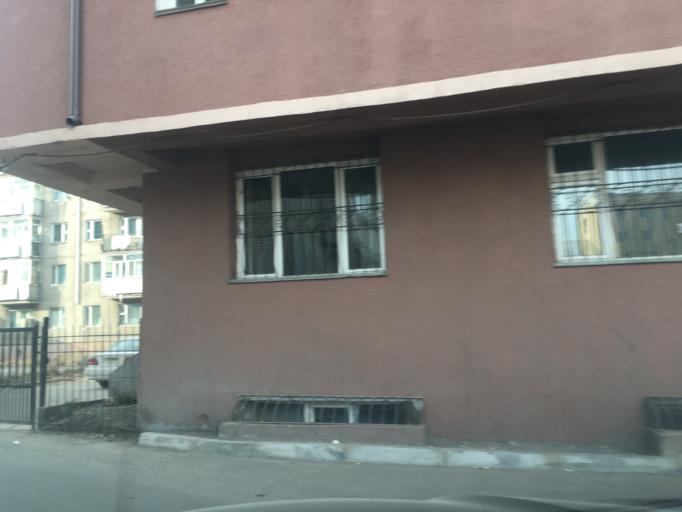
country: MN
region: Ulaanbaatar
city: Ulaanbaatar
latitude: 47.9118
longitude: 106.8886
